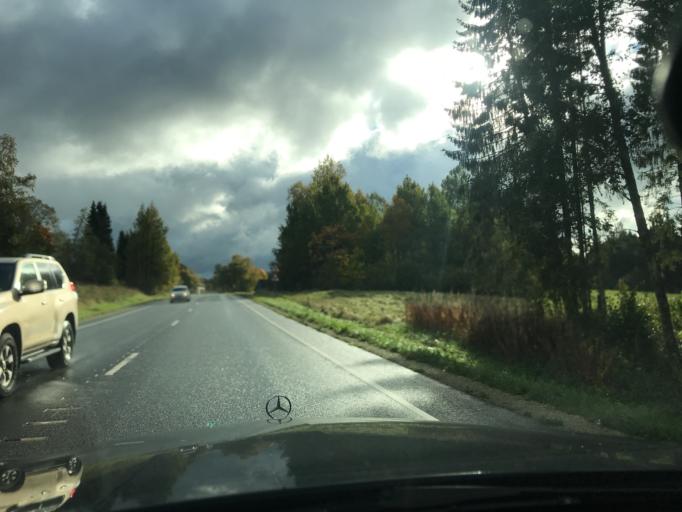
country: EE
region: Valgamaa
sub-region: Torva linn
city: Torva
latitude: 58.0084
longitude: 25.7551
